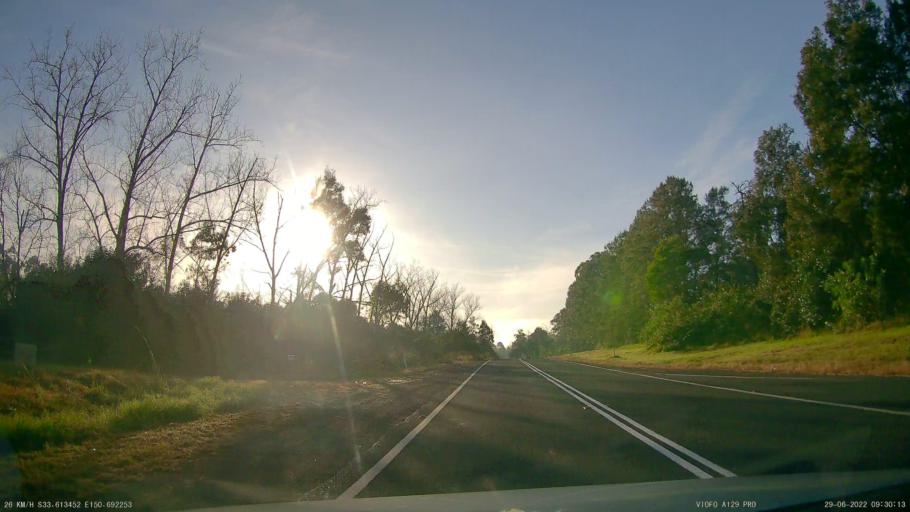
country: AU
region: New South Wales
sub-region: Hawkesbury
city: Richmond
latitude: -33.6133
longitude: 150.6925
